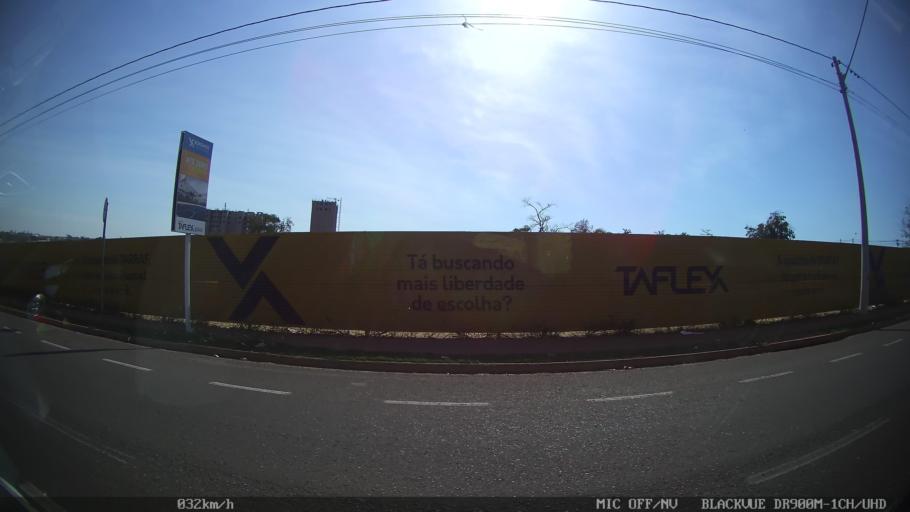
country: BR
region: Sao Paulo
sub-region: Sao Jose Do Rio Preto
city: Sao Jose do Rio Preto
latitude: -20.7912
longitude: -49.4215
